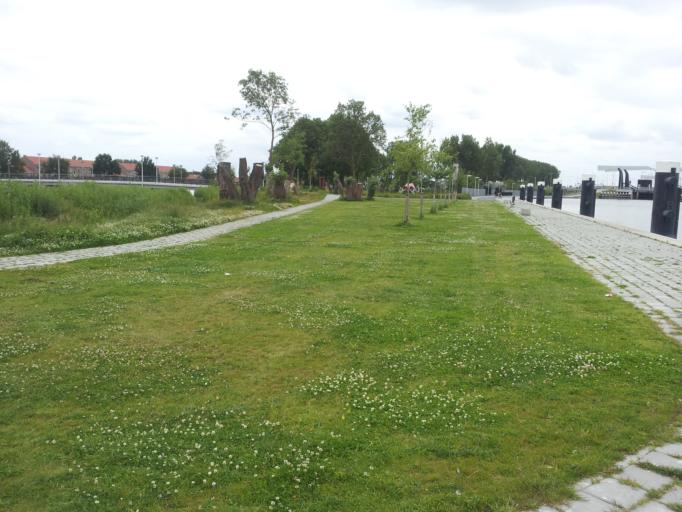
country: NL
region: South Holland
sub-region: Gemeente Gouda
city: Gouda
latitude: 52.0052
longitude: 4.6945
